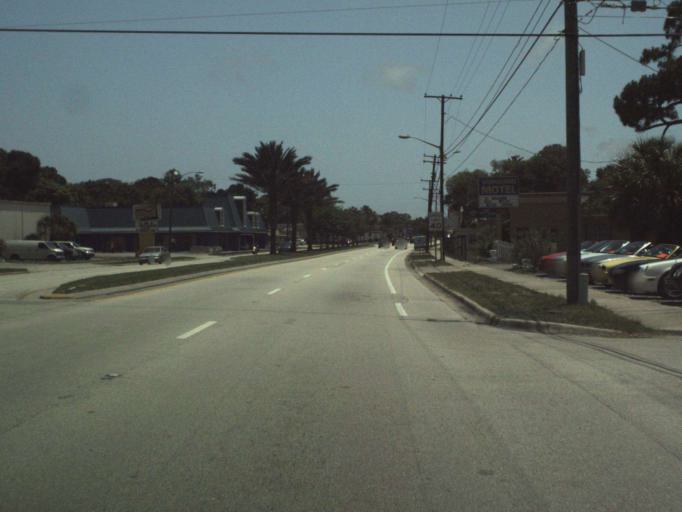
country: US
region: Florida
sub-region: Volusia County
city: Ormond Beach
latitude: 29.2670
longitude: -81.0534
